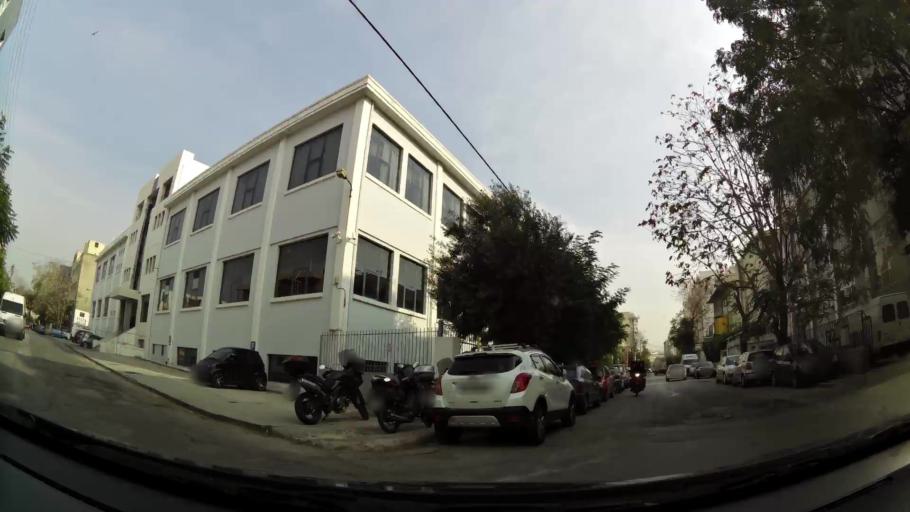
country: GR
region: Attica
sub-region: Nomarchia Athinas
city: Tavros
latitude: 37.9621
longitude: 23.6965
